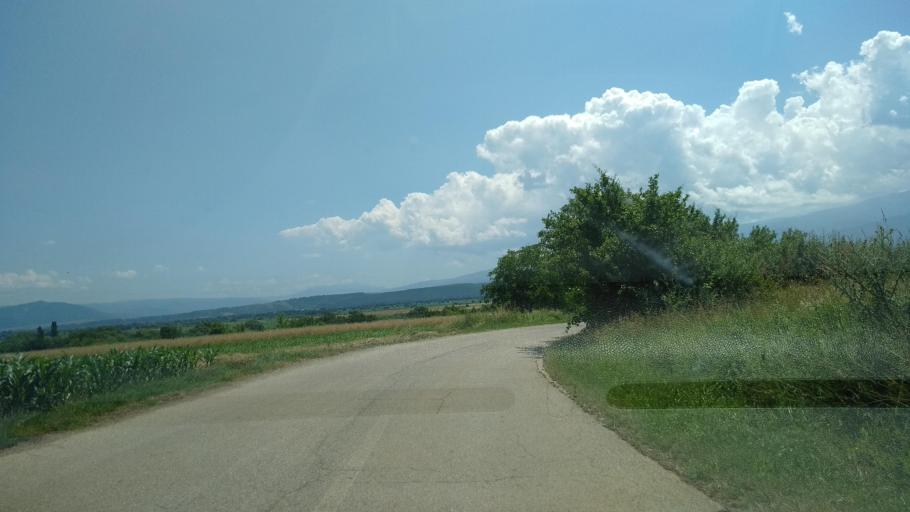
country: RO
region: Hunedoara
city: Densus
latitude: 45.5607
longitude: 22.8177
